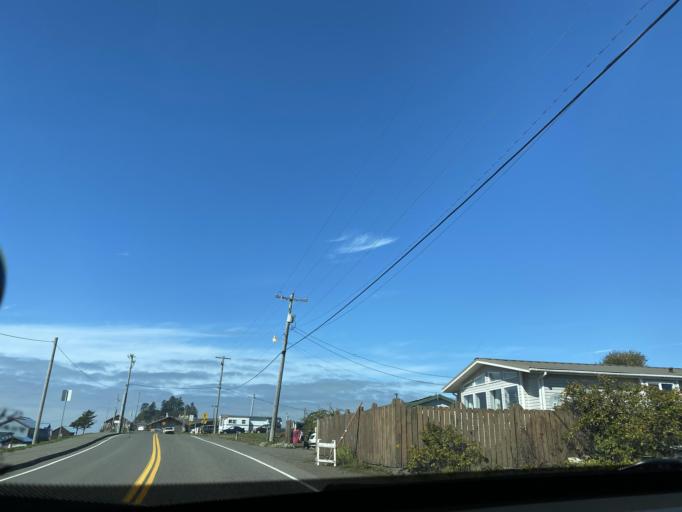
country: US
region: Washington
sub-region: Clallam County
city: Forks
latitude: 47.9074
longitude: -124.6346
